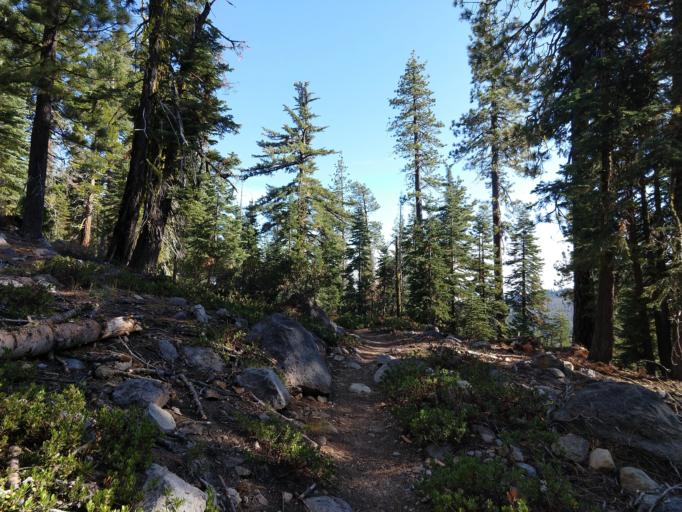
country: US
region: California
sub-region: Plumas County
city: Chester
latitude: 40.4478
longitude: -121.4022
